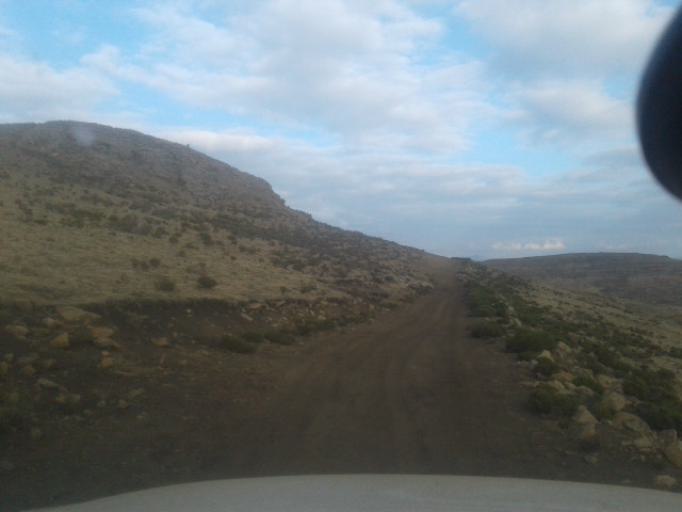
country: LS
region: Thaba-Tseka
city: Thaba-Tseka
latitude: -29.4139
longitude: 28.2705
